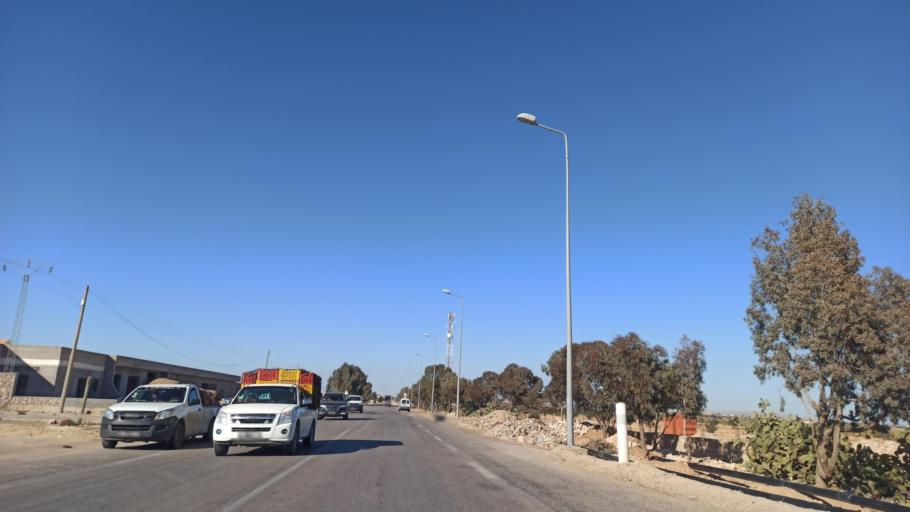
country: TN
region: Sidi Bu Zayd
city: Jilma
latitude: 35.2895
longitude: 9.4185
